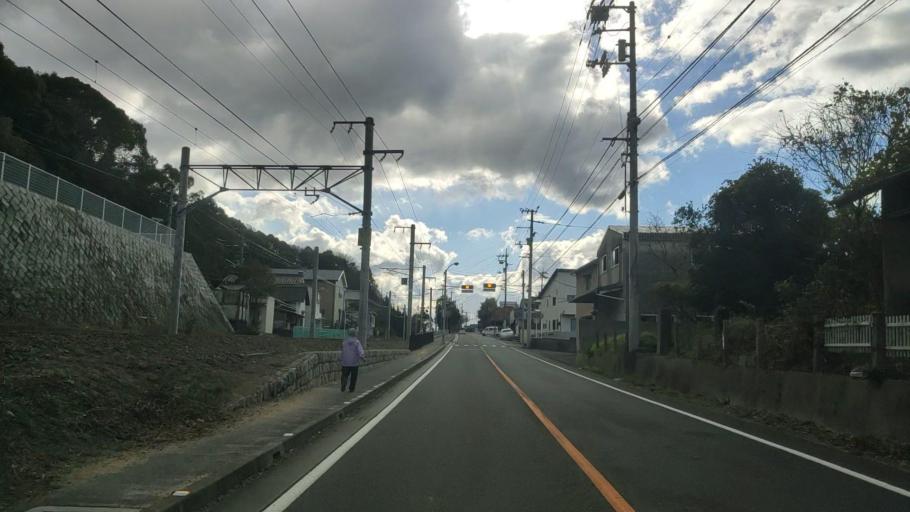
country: JP
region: Ehime
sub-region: Shikoku-chuo Shi
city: Matsuyama
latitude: 33.8804
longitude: 132.7023
